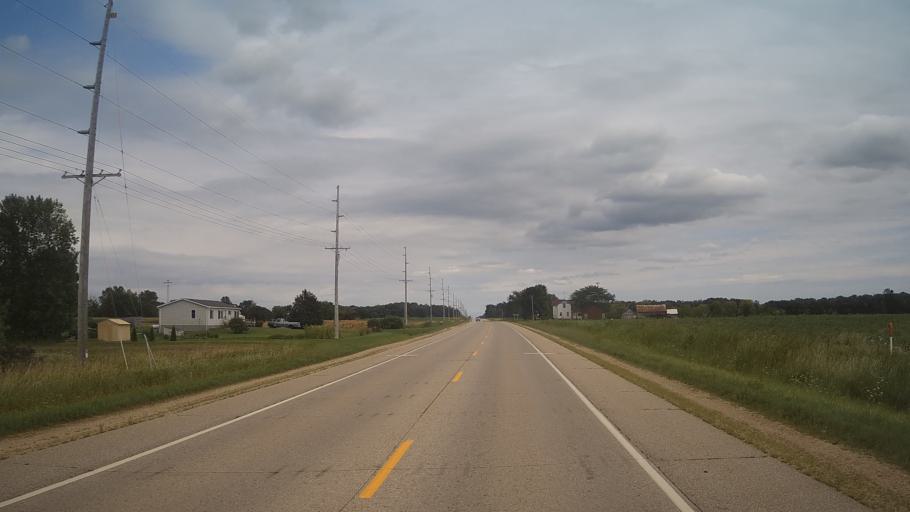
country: US
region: Wisconsin
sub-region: Waushara County
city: Redgranite
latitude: 44.0410
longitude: -89.0121
